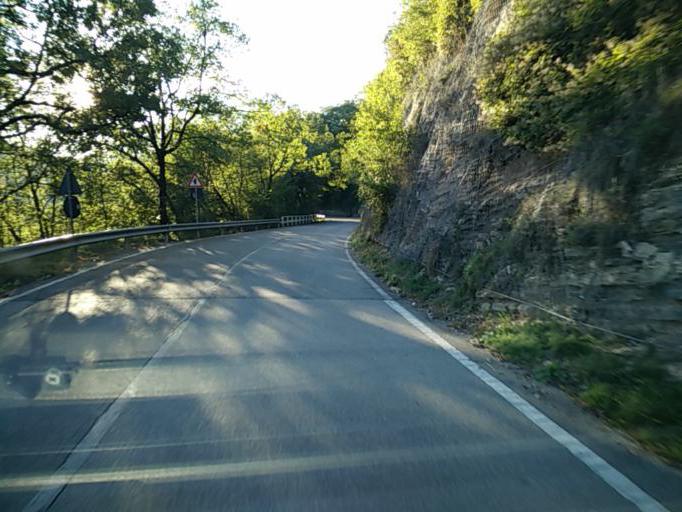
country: IT
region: Lombardy
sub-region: Provincia di Brescia
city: Gargnano
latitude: 45.6849
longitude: 10.6467
